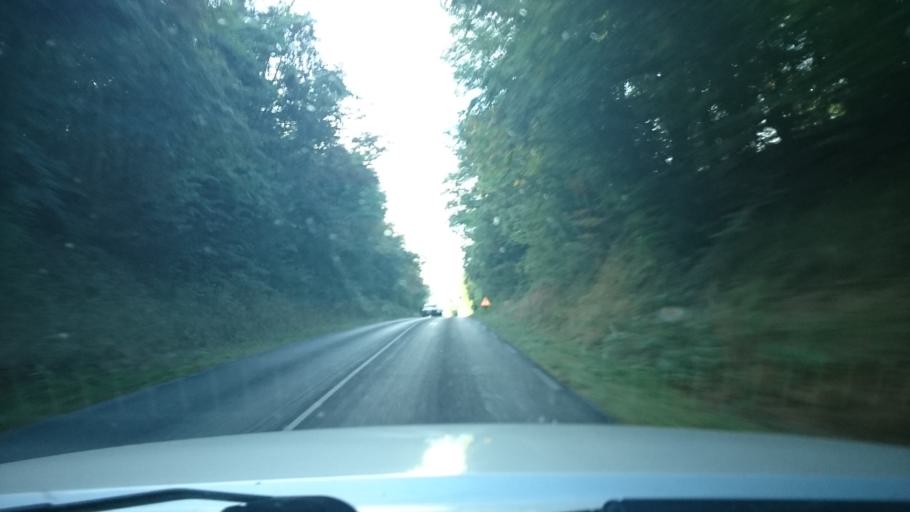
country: FR
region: Ile-de-France
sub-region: Departement de Seine-et-Marne
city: Samoreau
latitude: 48.4104
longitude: 2.7449
